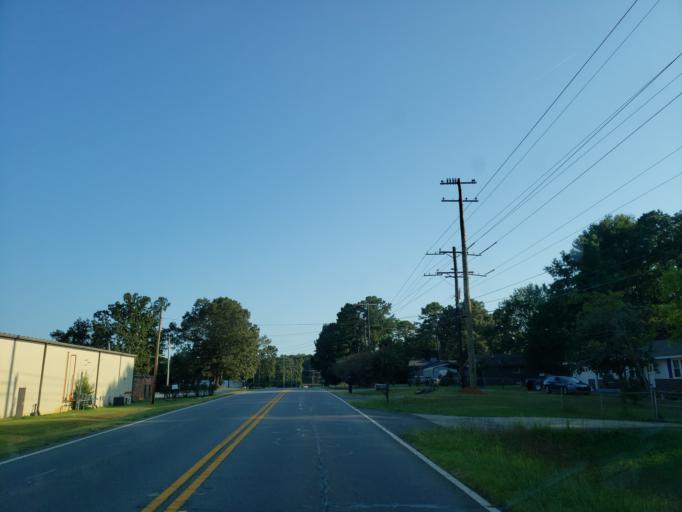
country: US
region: Georgia
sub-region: Murray County
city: Chatsworth
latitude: 34.7416
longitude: -84.8200
